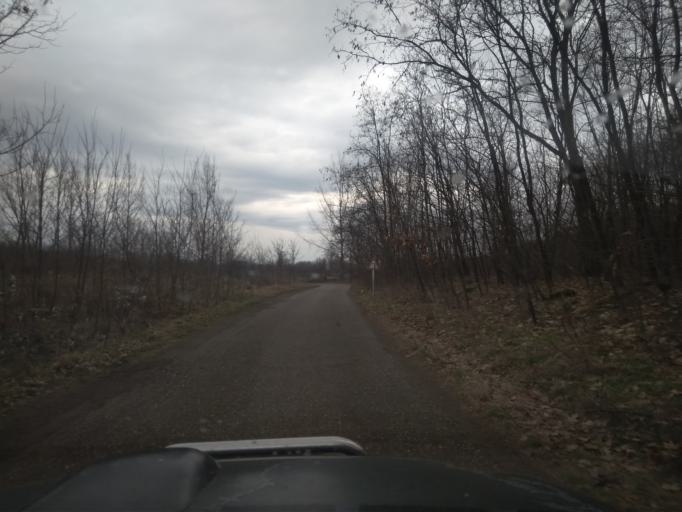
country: HU
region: Szabolcs-Szatmar-Bereg
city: Nyirpazony
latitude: 48.0144
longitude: 21.8105
